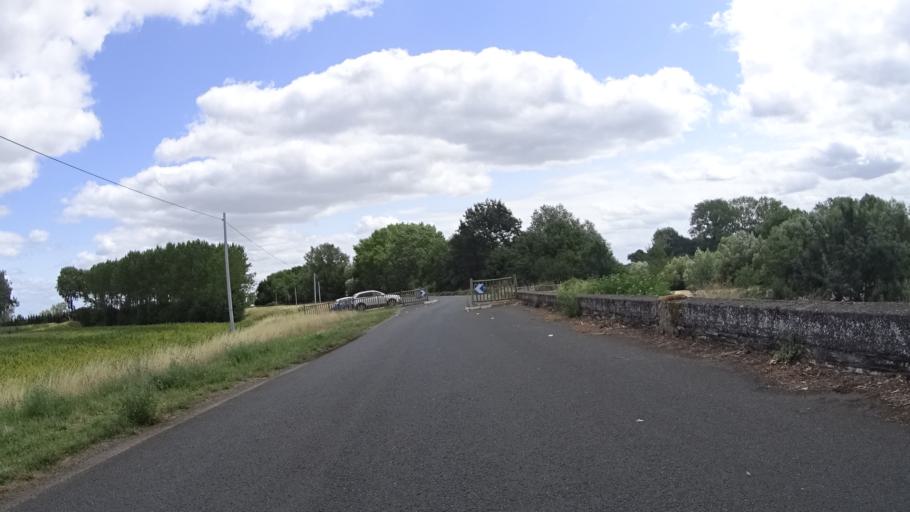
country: FR
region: Pays de la Loire
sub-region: Departement de Maine-et-Loire
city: Saint-Jean-des-Mauvrets
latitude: 47.4198
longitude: -0.4543
